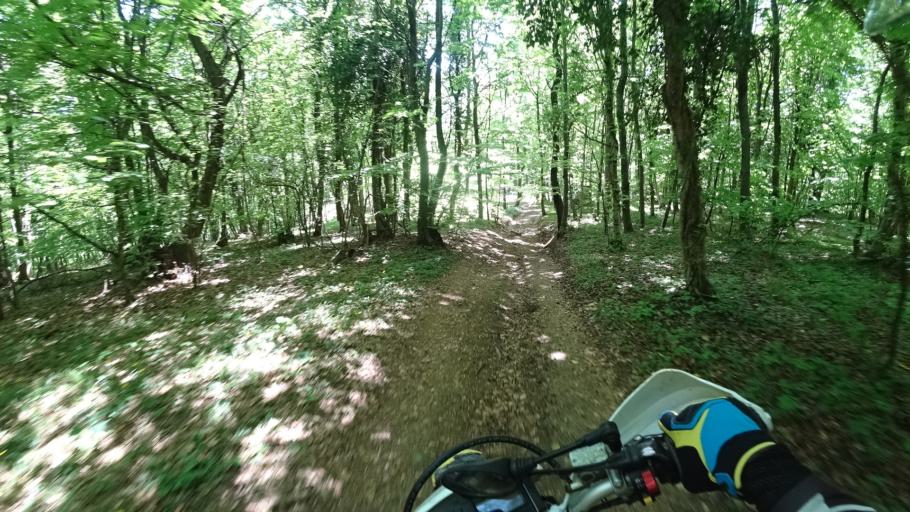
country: HR
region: Zagrebacka
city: Jablanovec
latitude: 45.8566
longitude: 15.8647
